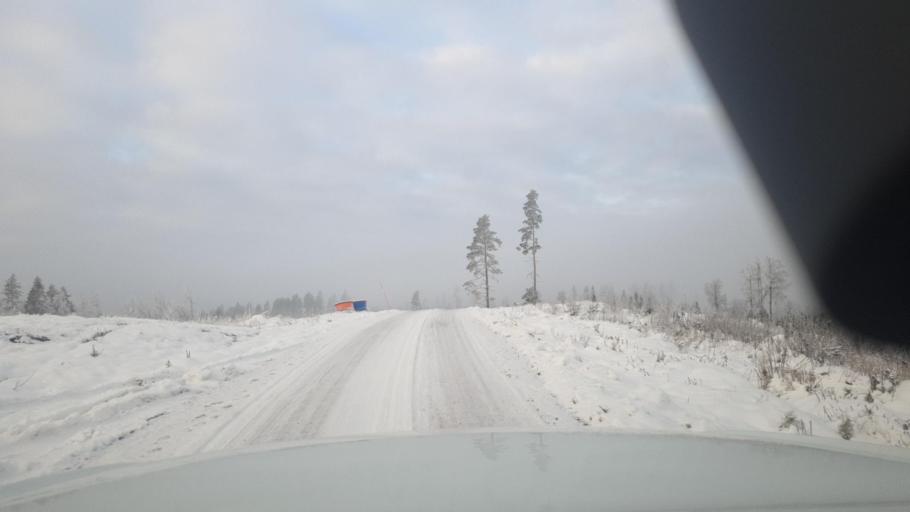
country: SE
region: Vaermland
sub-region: Torsby Kommun
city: Torsby
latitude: 59.9545
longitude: 12.7745
